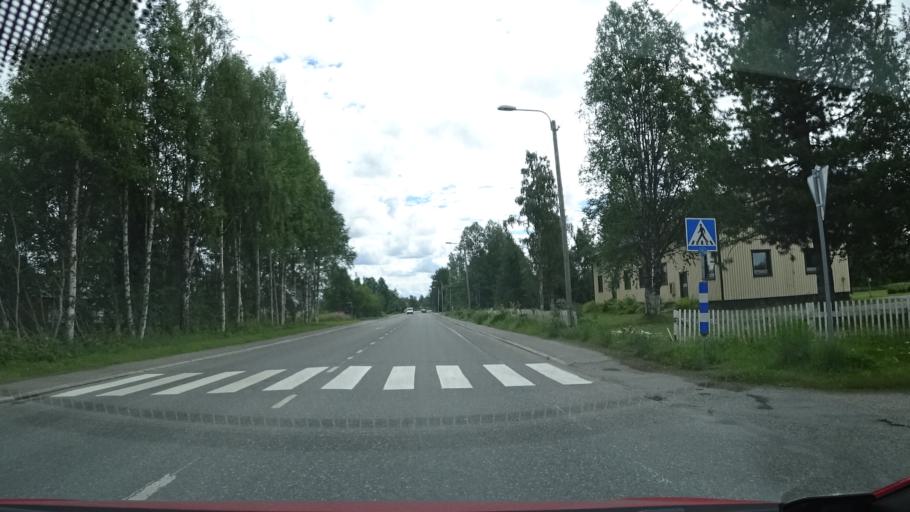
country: FI
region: Lapland
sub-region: Tunturi-Lappi
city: Kittilae
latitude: 67.6631
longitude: 24.8980
